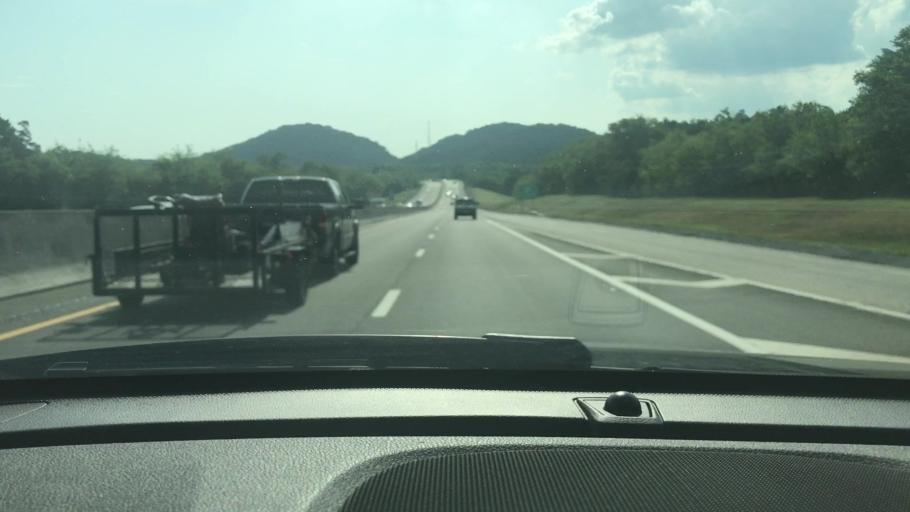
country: US
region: Tennessee
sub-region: Davidson County
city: Nashville
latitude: 36.2340
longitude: -86.8179
